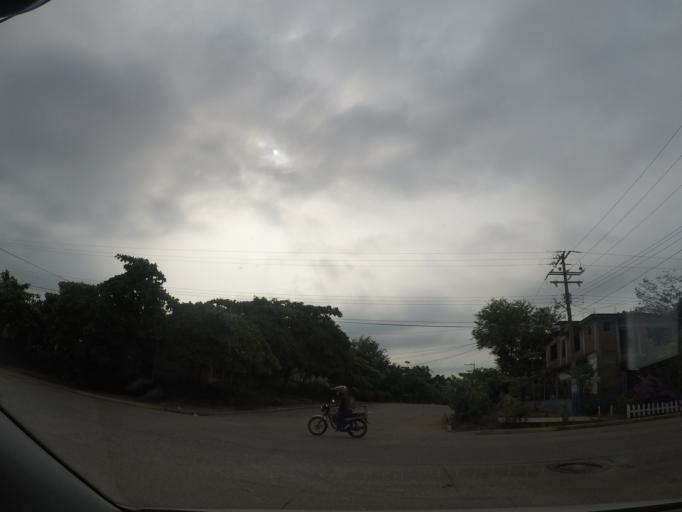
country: MX
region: Oaxaca
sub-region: Santa Maria Petapa
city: Llano Suchiapa
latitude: 16.8688
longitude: -95.0475
